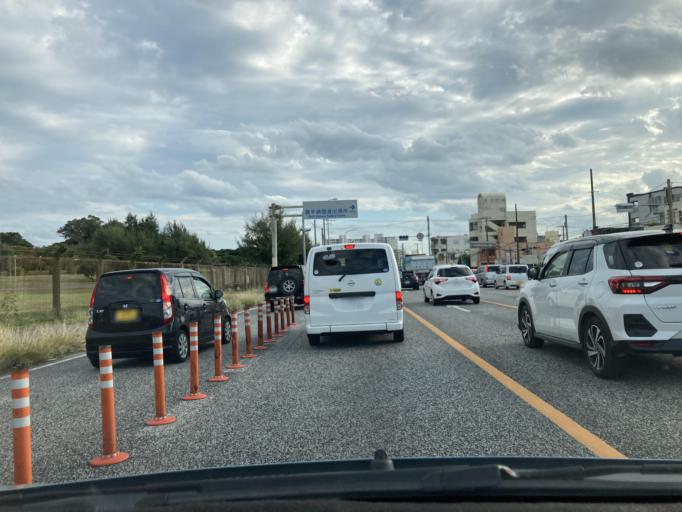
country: JP
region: Okinawa
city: Chatan
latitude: 26.3314
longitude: 127.7518
